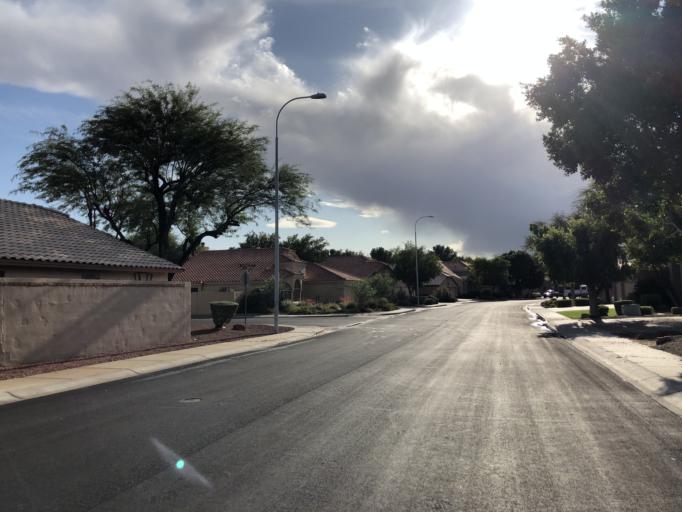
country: US
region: Arizona
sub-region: Maricopa County
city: Guadalupe
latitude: 33.3115
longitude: -111.9218
